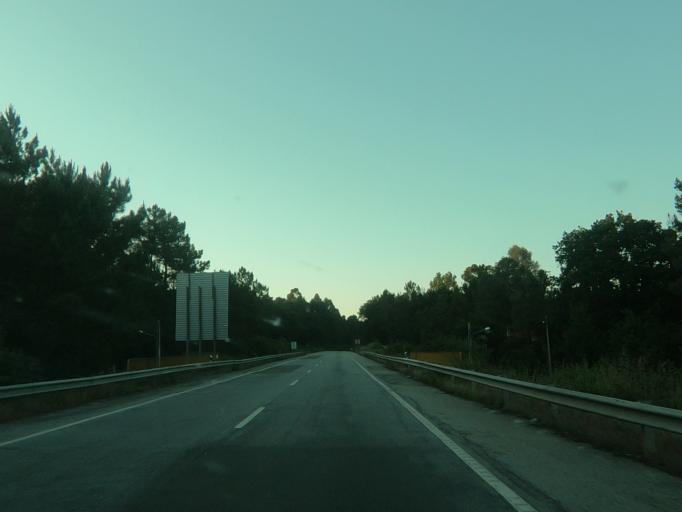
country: PT
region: Viseu
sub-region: Viseu
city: Rio de Loba
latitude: 40.6627
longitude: -7.8624
